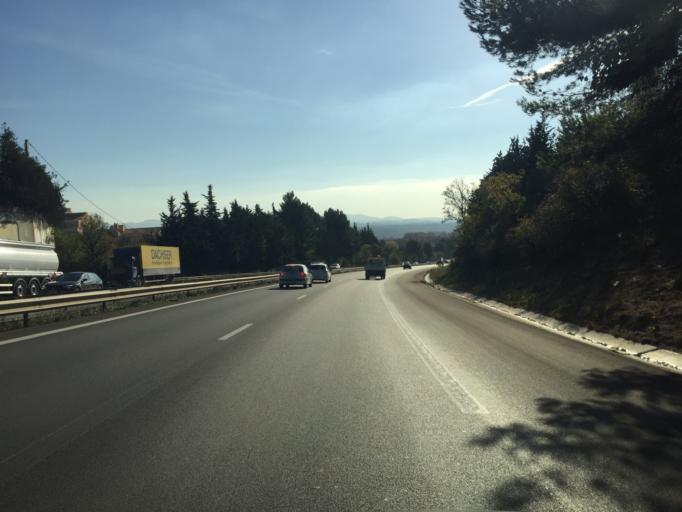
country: FR
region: Provence-Alpes-Cote d'Azur
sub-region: Departement des Bouches-du-Rhone
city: Aix-en-Provence
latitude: 43.5390
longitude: 5.4328
